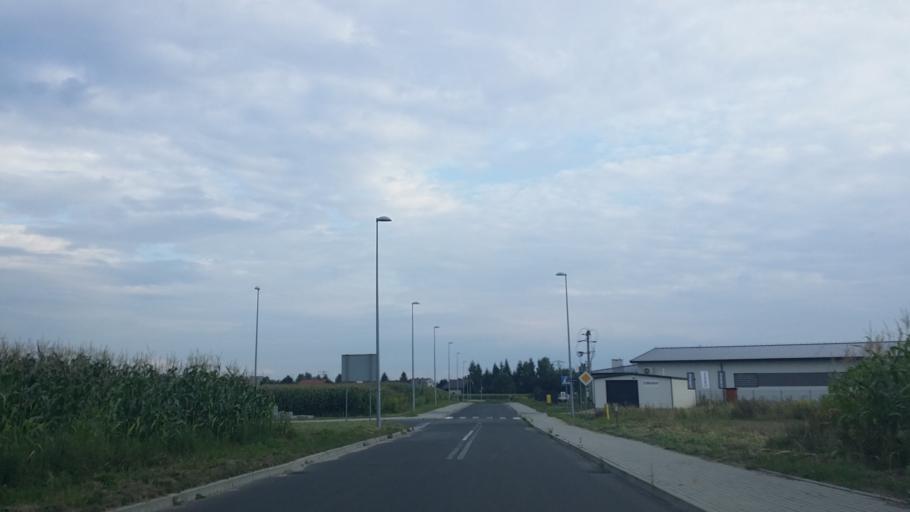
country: PL
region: Lesser Poland Voivodeship
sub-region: Powiat oswiecimski
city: Zator
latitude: 49.9945
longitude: 19.4253
